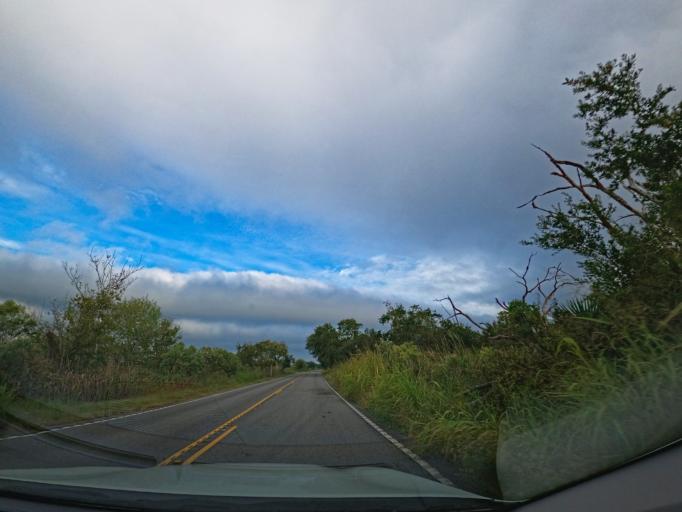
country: US
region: Louisiana
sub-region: Terrebonne Parish
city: Dulac
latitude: 29.3490
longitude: -90.6983
